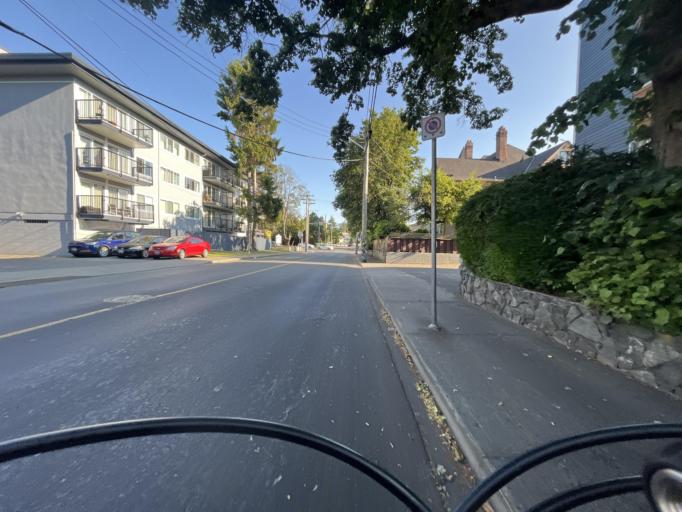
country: CA
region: British Columbia
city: Victoria
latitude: 48.4252
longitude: -123.3456
